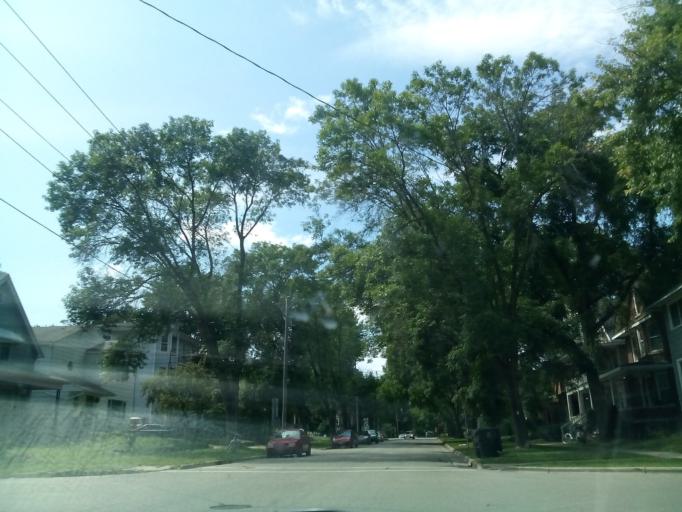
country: US
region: Wisconsin
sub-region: Dane County
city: Madison
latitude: 43.0632
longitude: -89.4023
